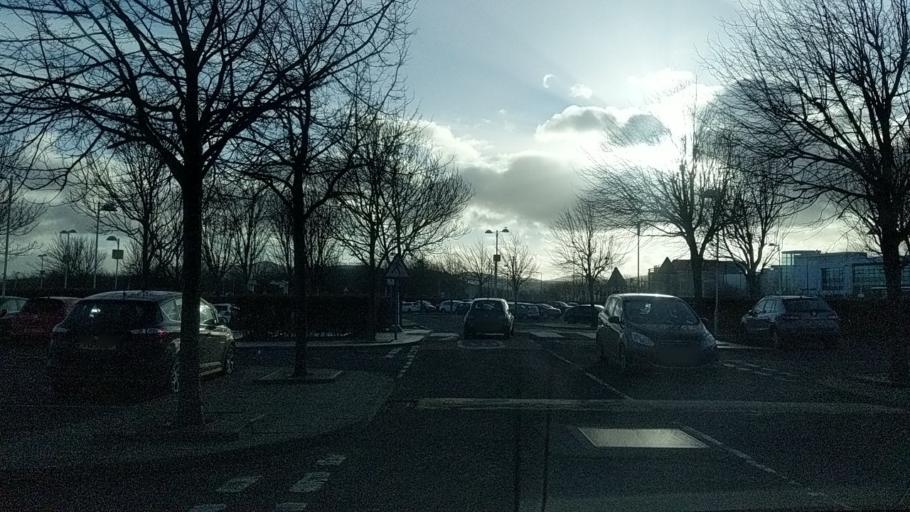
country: GB
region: Scotland
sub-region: Edinburgh
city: Currie
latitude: 55.9388
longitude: -3.3181
